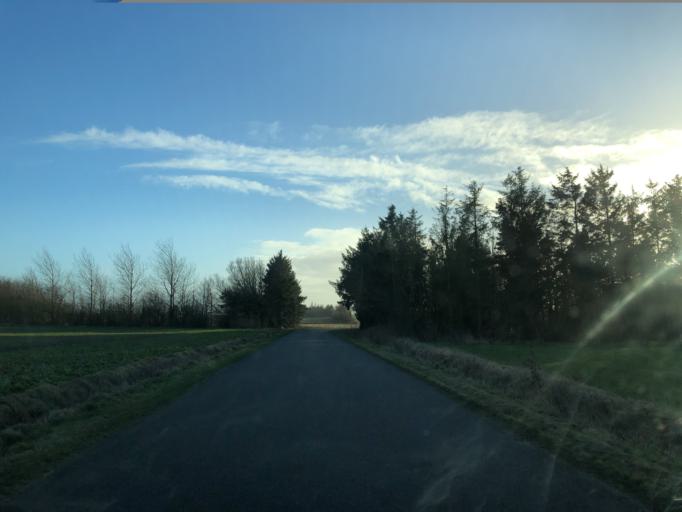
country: DK
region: Central Jutland
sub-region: Holstebro Kommune
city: Ulfborg
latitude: 56.3086
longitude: 8.2124
